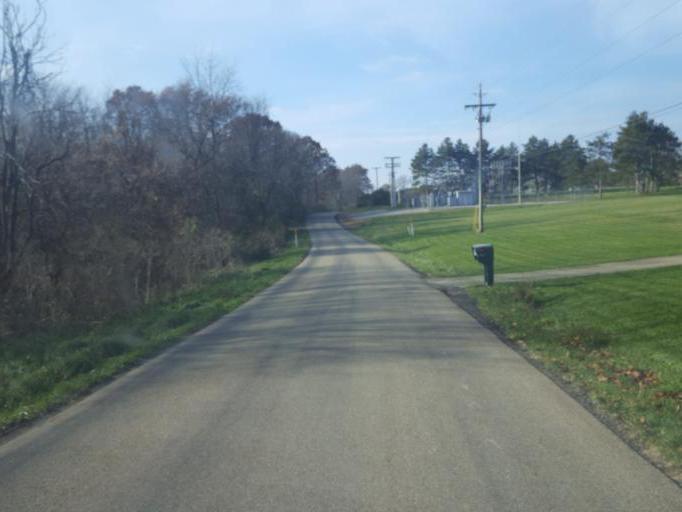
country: US
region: Ohio
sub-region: Knox County
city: Gambier
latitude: 40.3900
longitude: -82.4051
